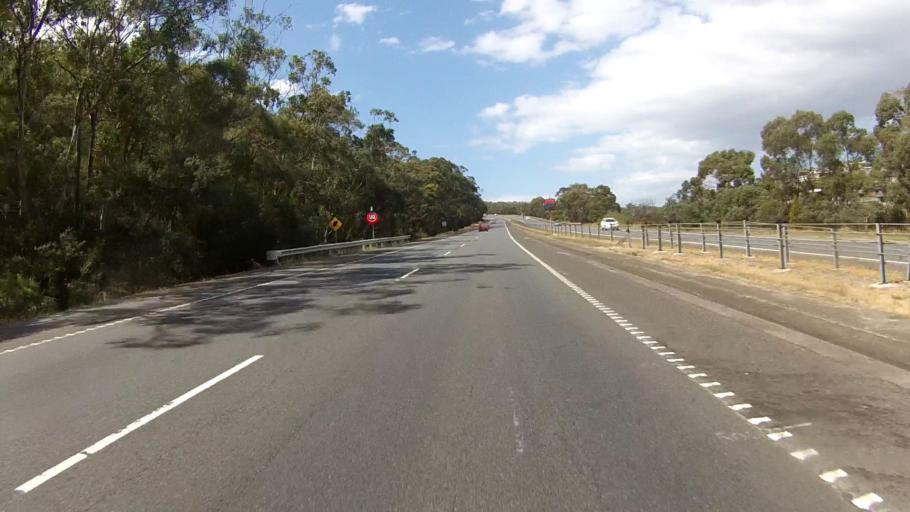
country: AU
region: Tasmania
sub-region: Clarence
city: Warrane
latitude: -42.8551
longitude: 147.4037
